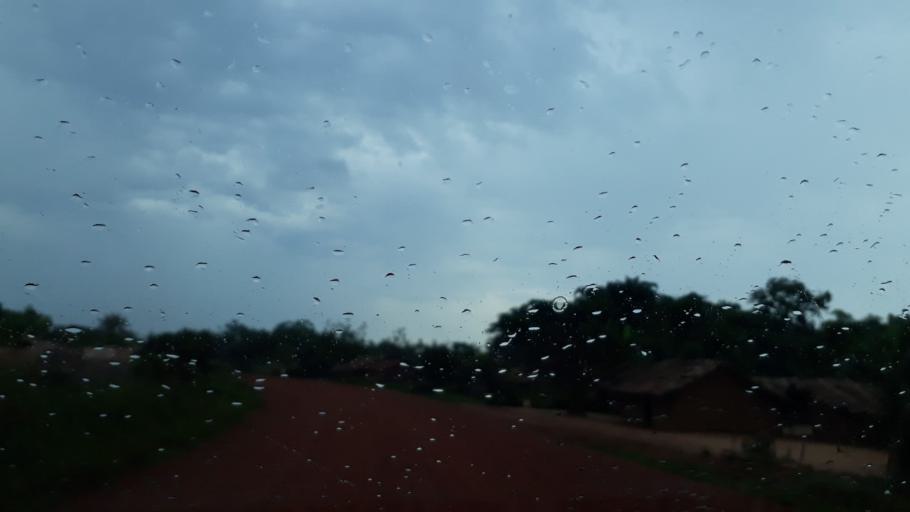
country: CD
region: Eastern Province
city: Kisangani
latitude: 0.4698
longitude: 25.4264
